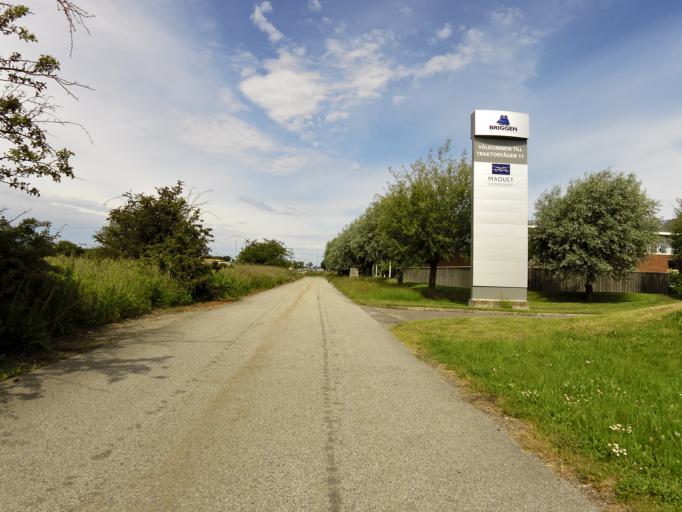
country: SE
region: Skane
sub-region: Lunds Kommun
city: Lund
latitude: 55.7160
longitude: 13.1603
